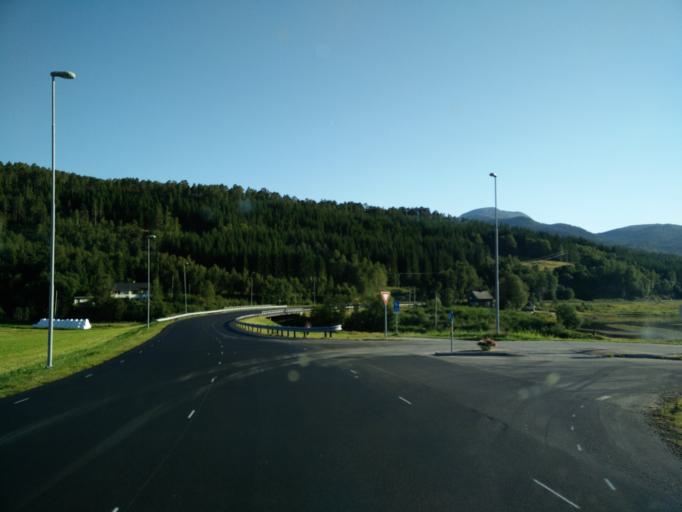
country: NO
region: More og Romsdal
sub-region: Halsa
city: Liaboen
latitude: 63.0863
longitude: 8.3492
